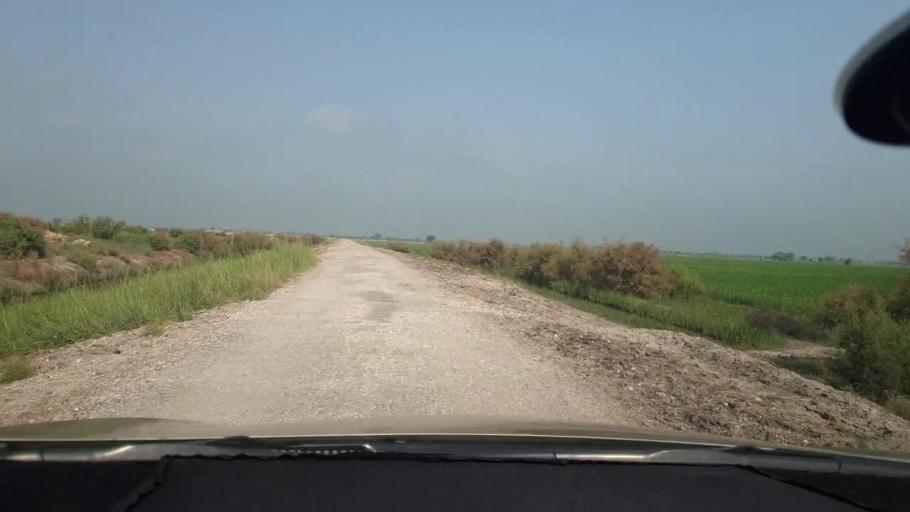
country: PK
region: Sindh
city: Kambar
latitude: 27.5333
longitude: 68.0659
